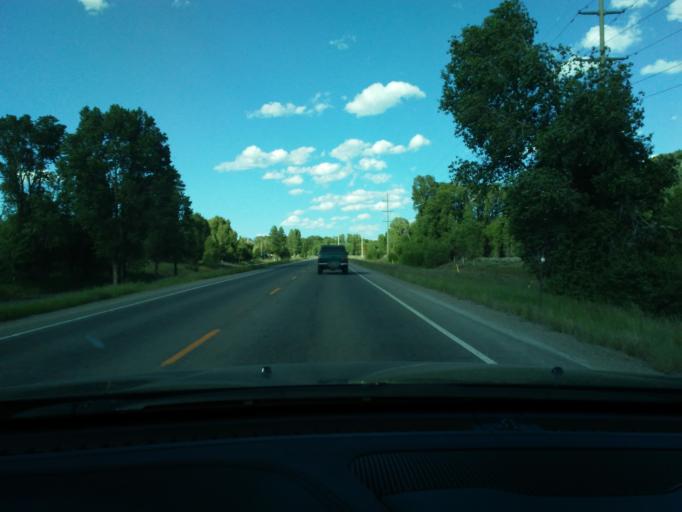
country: US
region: Wyoming
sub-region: Teton County
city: Moose Wilson Road
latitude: 43.5377
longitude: -110.8277
